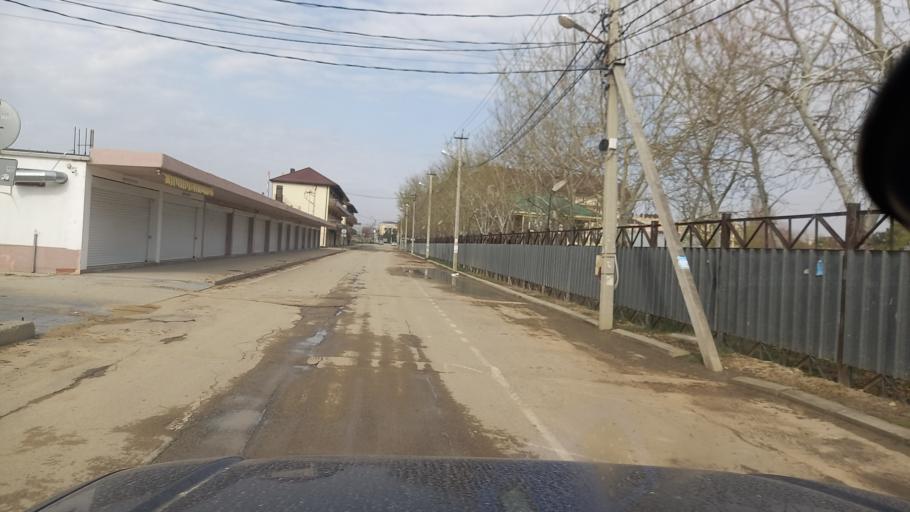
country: RU
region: Krasnodarskiy
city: Vityazevo
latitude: 44.9857
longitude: 37.2492
